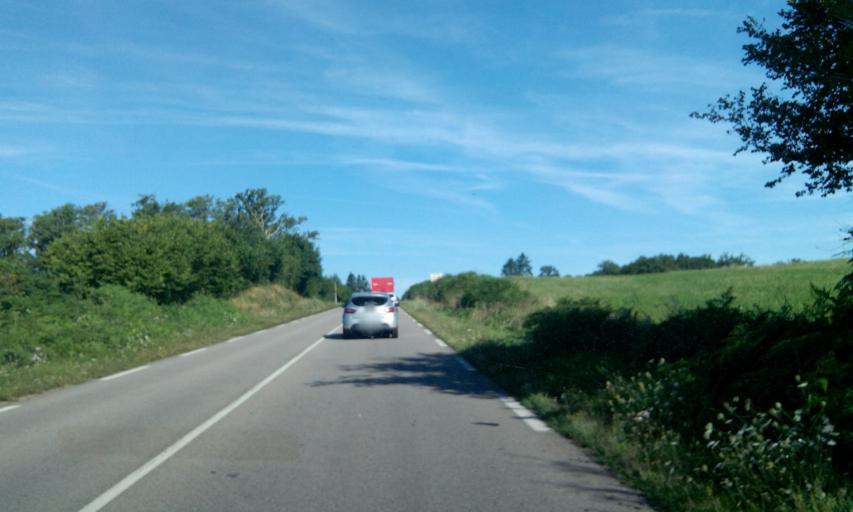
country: FR
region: Limousin
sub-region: Departement de la Haute-Vienne
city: Saint-Leonard-de-Noblat
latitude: 45.8425
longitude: 1.4631
